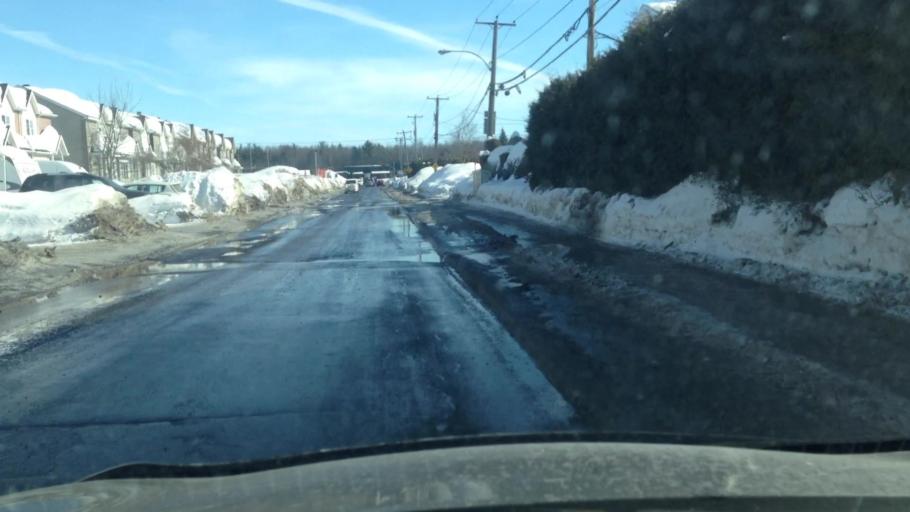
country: CA
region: Quebec
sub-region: Laurentides
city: Saint-Jerome
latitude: 45.7734
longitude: -73.9738
